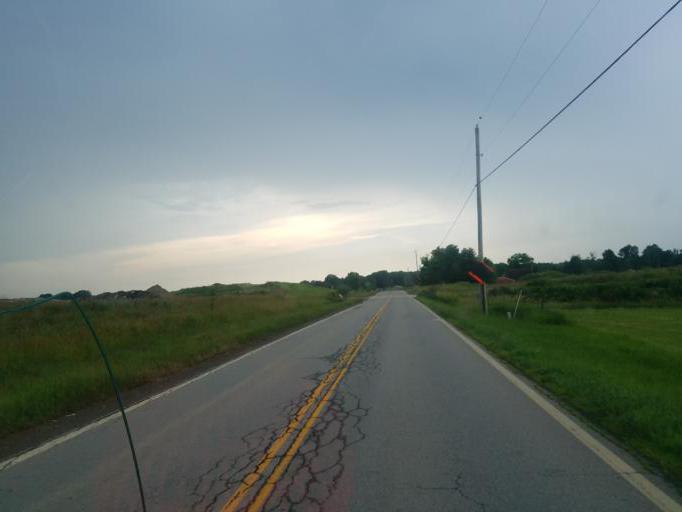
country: US
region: Ohio
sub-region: Wayne County
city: Rittman
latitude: 40.9456
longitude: -81.7578
